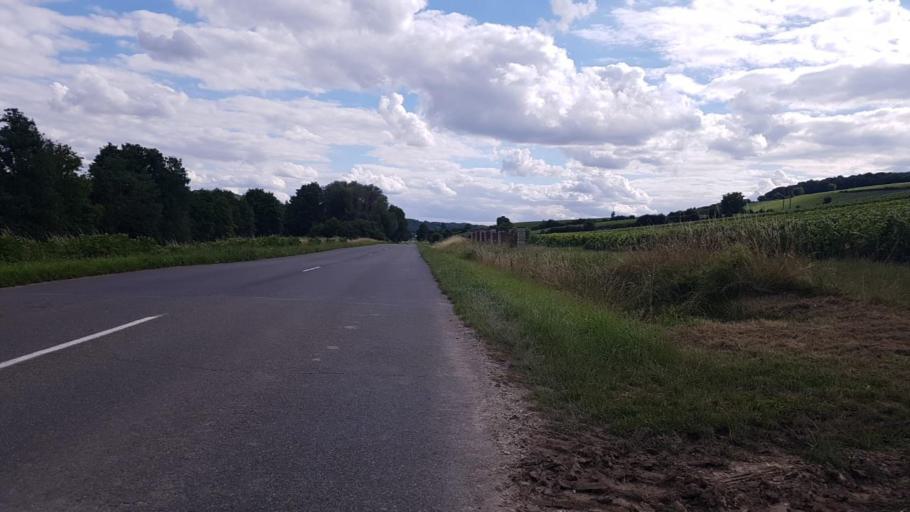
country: FR
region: Picardie
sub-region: Departement de l'Aisne
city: Crezancy
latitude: 49.0636
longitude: 3.4783
